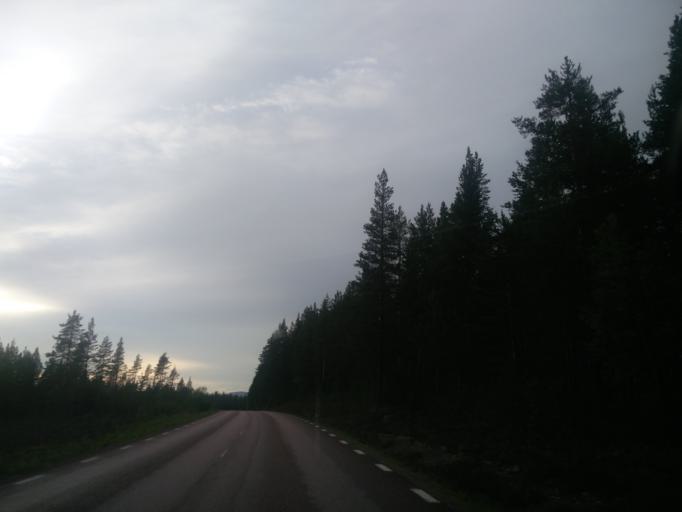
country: NO
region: Hedmark
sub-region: Trysil
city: Innbygda
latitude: 61.7741
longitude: 12.9483
